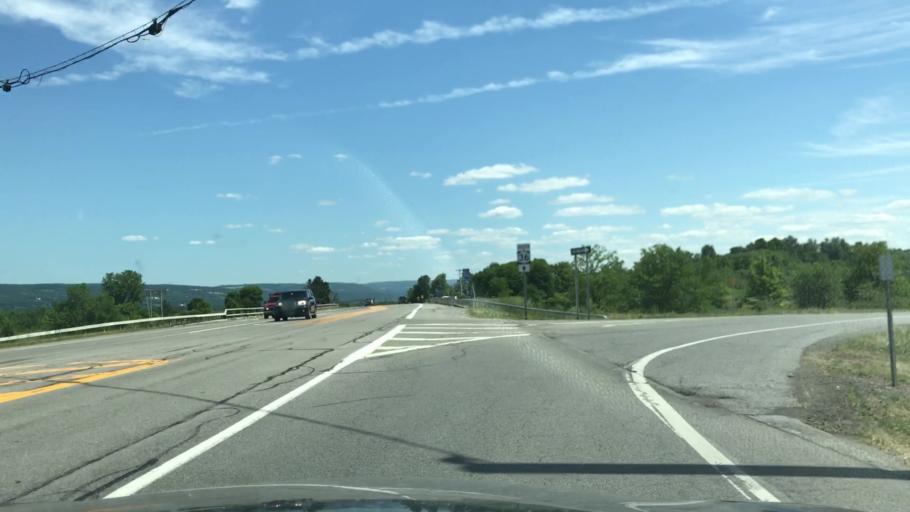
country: US
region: New York
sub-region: Livingston County
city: Mount Morris
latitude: 42.6719
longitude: -77.8129
